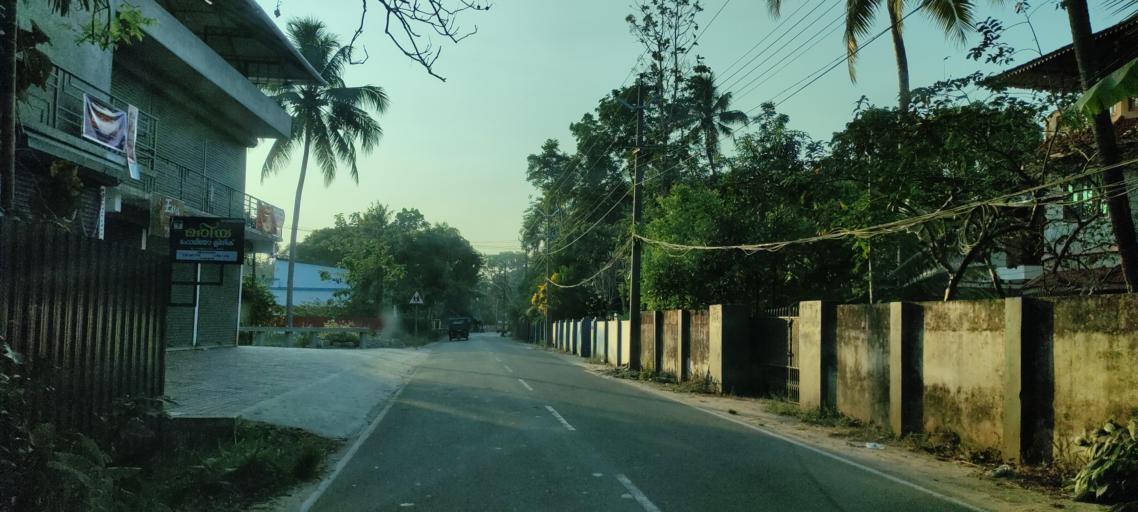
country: IN
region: Kerala
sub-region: Alappuzha
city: Kutiatodu
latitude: 9.7731
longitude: 76.3495
